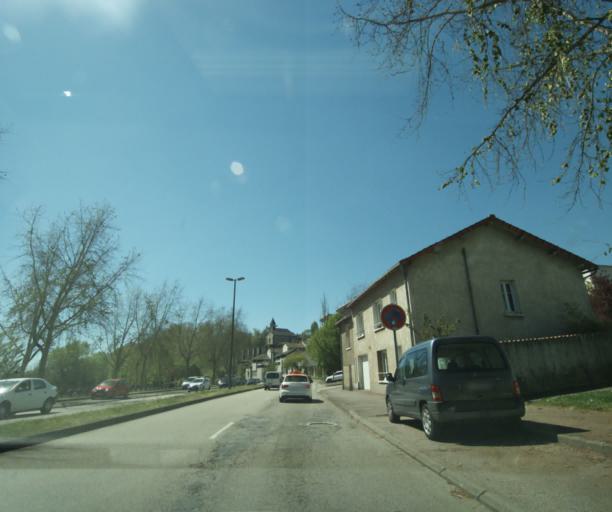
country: FR
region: Limousin
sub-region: Departement de la Haute-Vienne
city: Limoges
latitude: 45.8305
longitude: 1.2714
